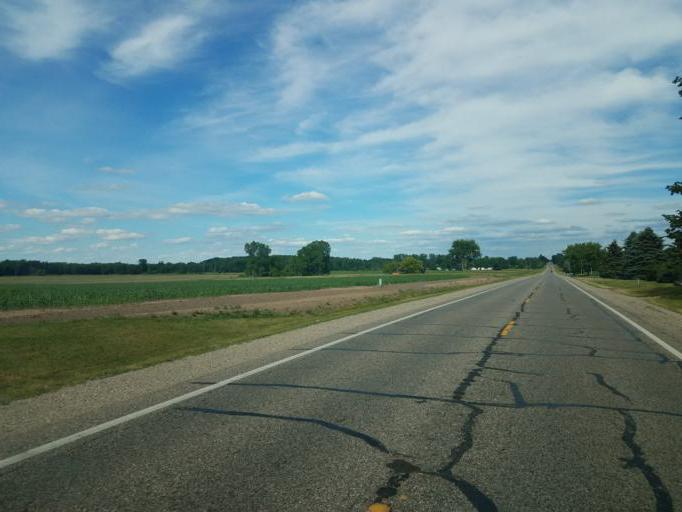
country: US
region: Michigan
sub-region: Eaton County
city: Charlotte
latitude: 42.5682
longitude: -84.9102
